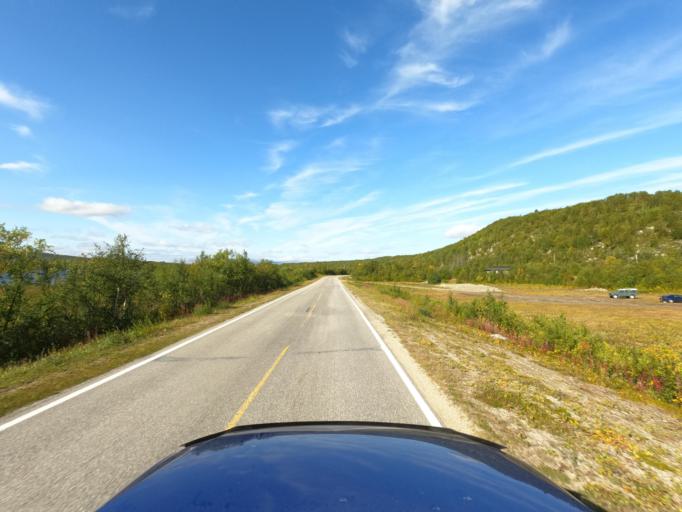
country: NO
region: Finnmark Fylke
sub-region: Porsanger
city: Lakselv
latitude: 69.7583
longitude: 25.2092
